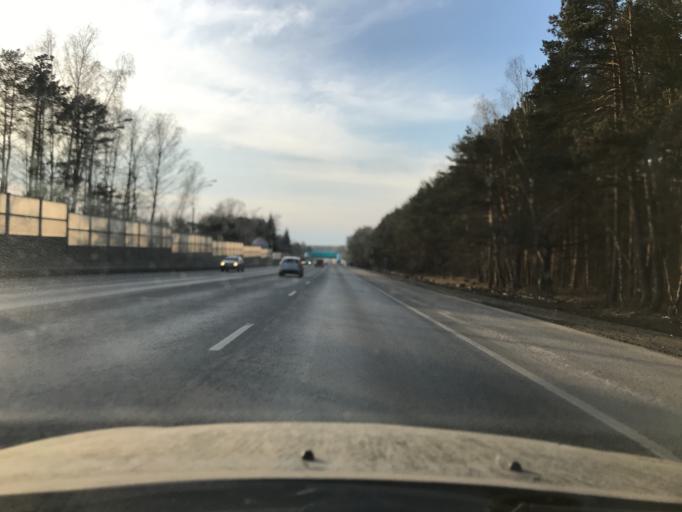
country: RU
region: Kaluga
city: Mstikhino
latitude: 54.5286
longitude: 36.1750
